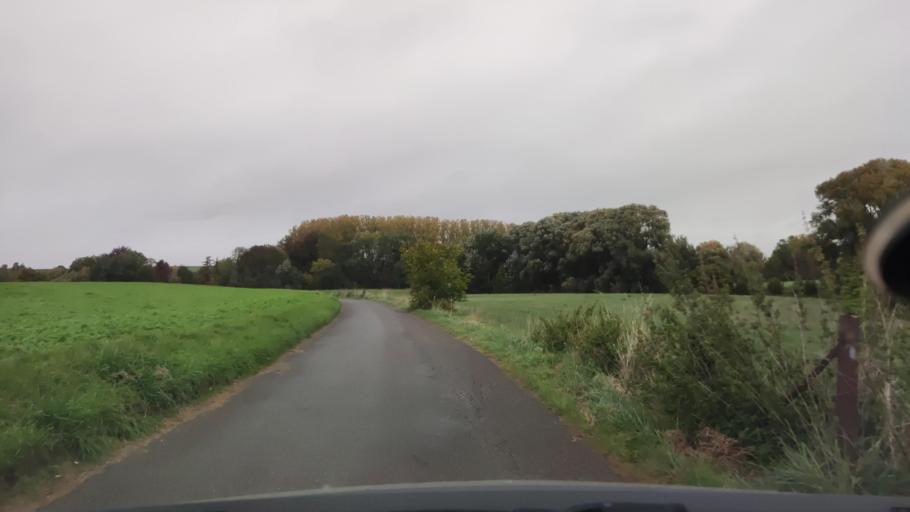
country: BE
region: Wallonia
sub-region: Province du Brabant Wallon
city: Jodoigne
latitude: 50.7475
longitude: 4.8714
